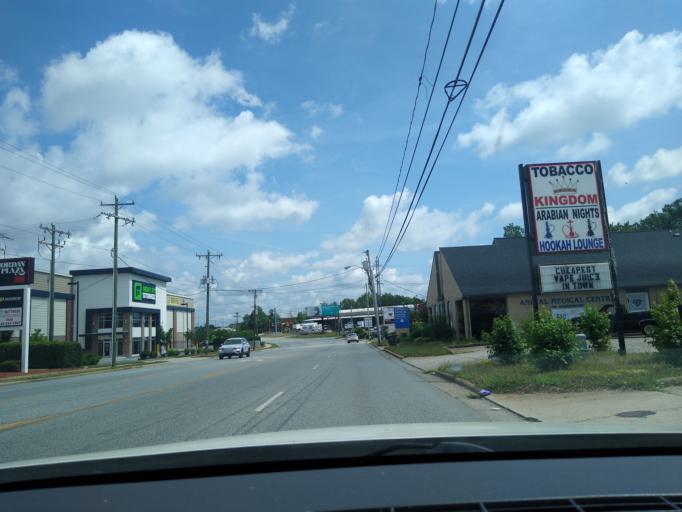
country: US
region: North Carolina
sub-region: Guilford County
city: Greensboro
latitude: 36.0675
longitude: -79.8678
